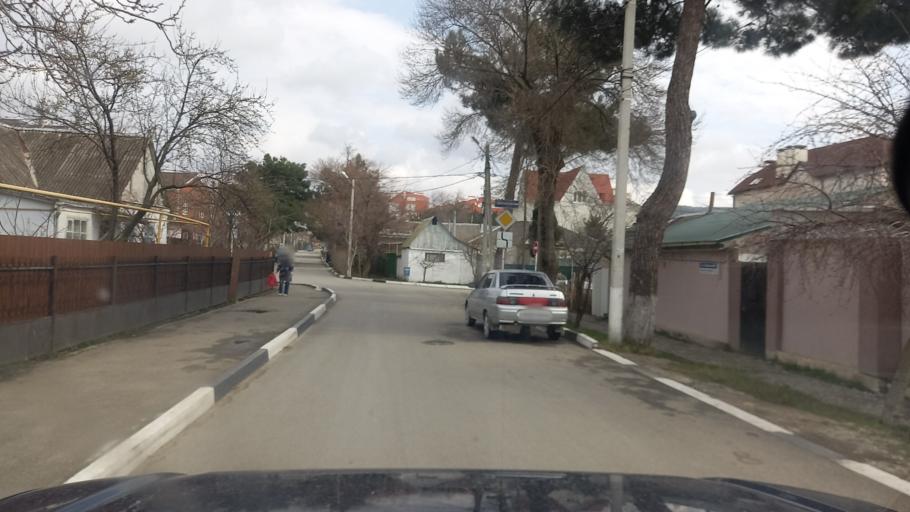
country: RU
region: Krasnodarskiy
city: Gelendzhik
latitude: 44.5590
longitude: 38.0881
